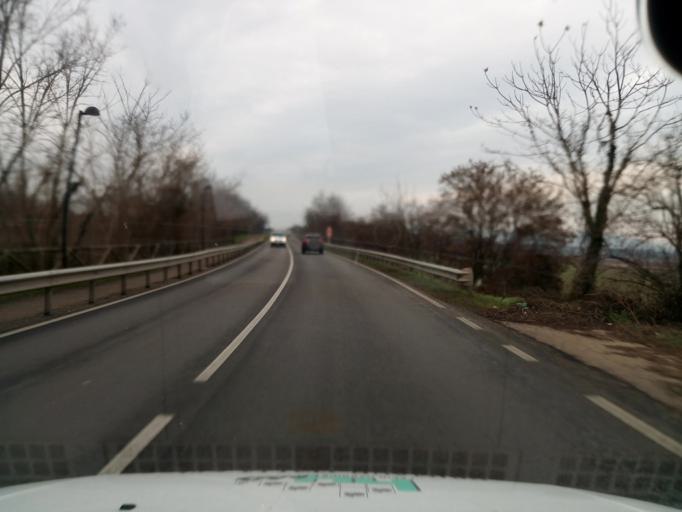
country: IT
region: Veneto
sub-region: Provincia di Vicenza
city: Montebello Vicentino
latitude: 45.4598
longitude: 11.3899
